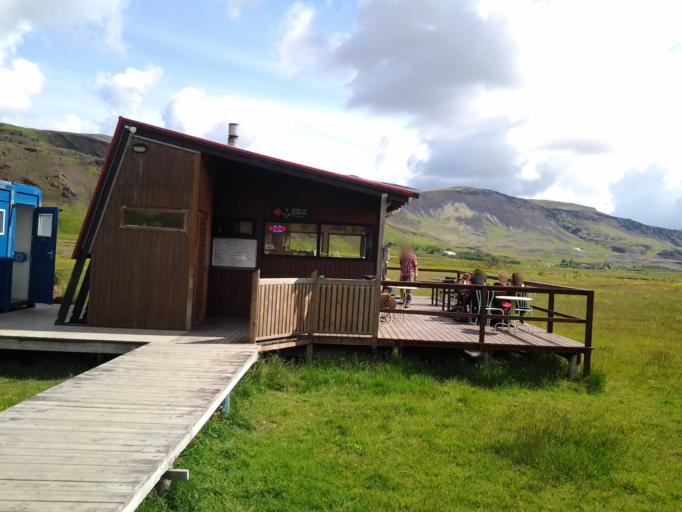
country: IS
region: South
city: Hveragerdi
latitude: 64.0222
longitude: -21.2112
